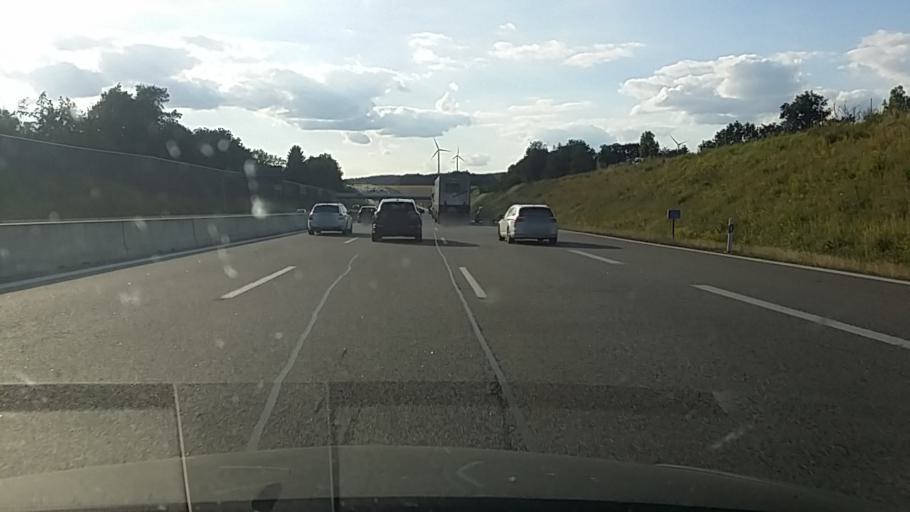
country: DE
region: Bavaria
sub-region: Upper Bavaria
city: Odelzhausen
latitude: 48.3102
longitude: 11.2040
